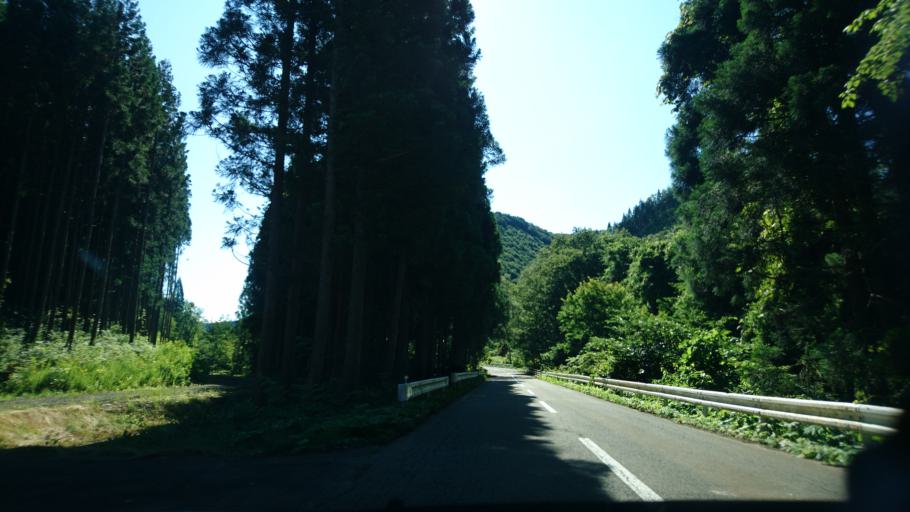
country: JP
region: Akita
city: Kakunodatemachi
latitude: 39.7061
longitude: 140.5918
